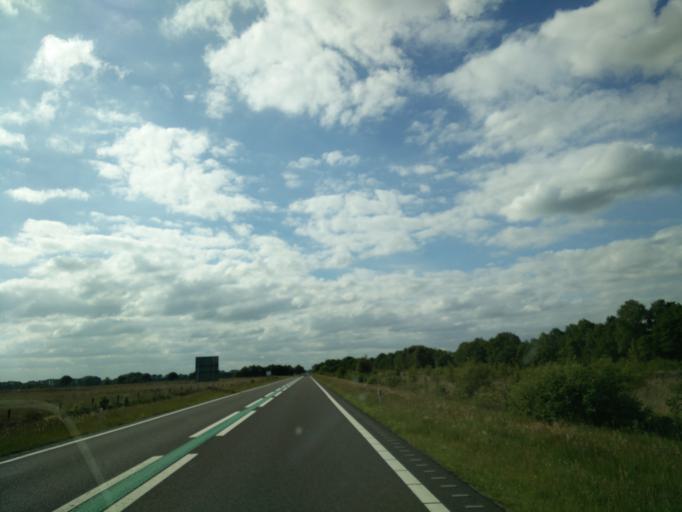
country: NL
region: Drenthe
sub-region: Gemeente Assen
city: Assen
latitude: 52.8375
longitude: 6.5917
